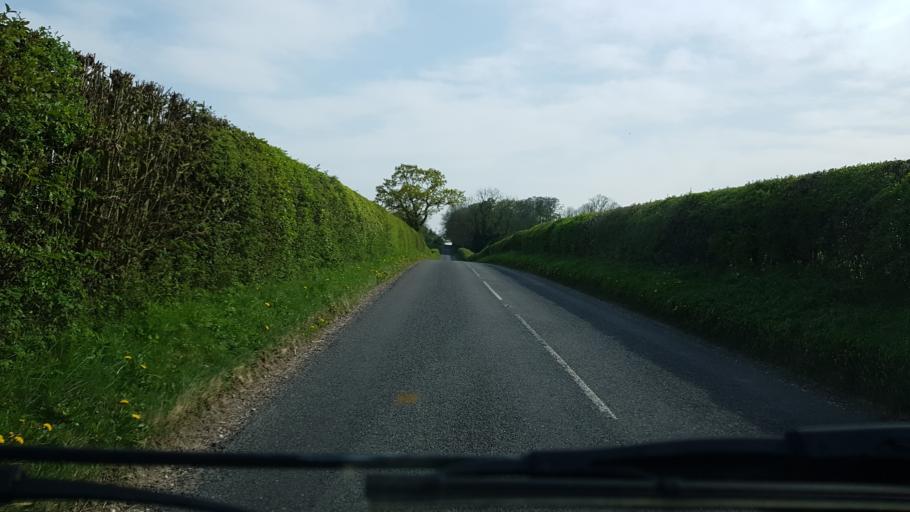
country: GB
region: England
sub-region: Hampshire
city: Overton
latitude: 51.2786
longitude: -1.2629
